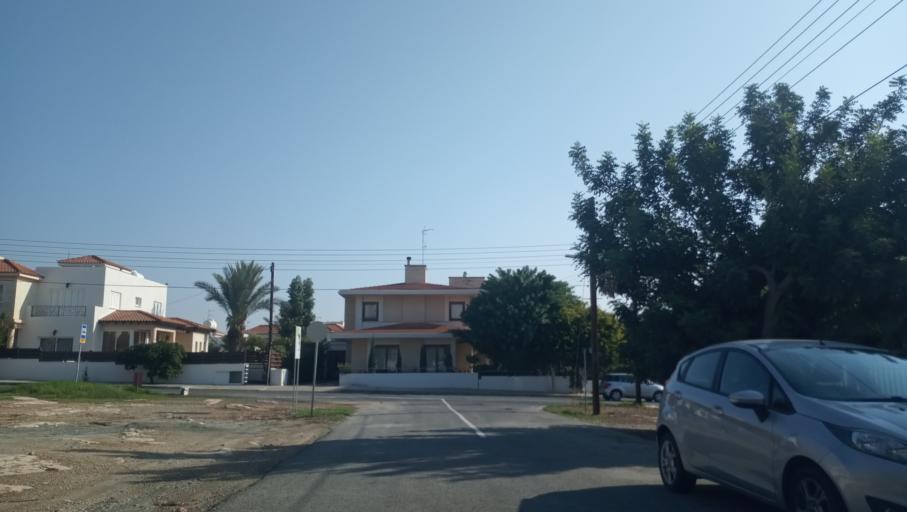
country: CY
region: Lefkosia
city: Nicosia
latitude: 35.1435
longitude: 33.3898
